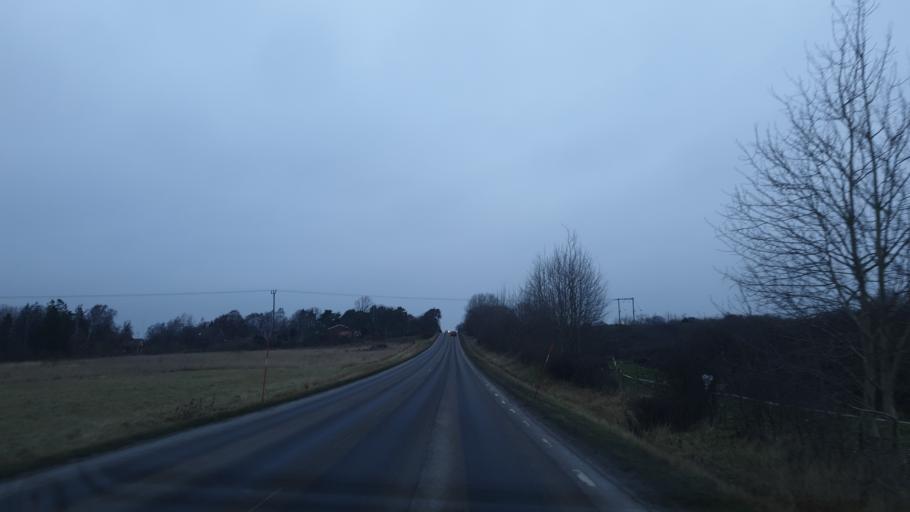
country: SE
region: Blekinge
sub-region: Karlskrona Kommun
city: Jaemjoe
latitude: 56.1473
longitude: 15.7588
